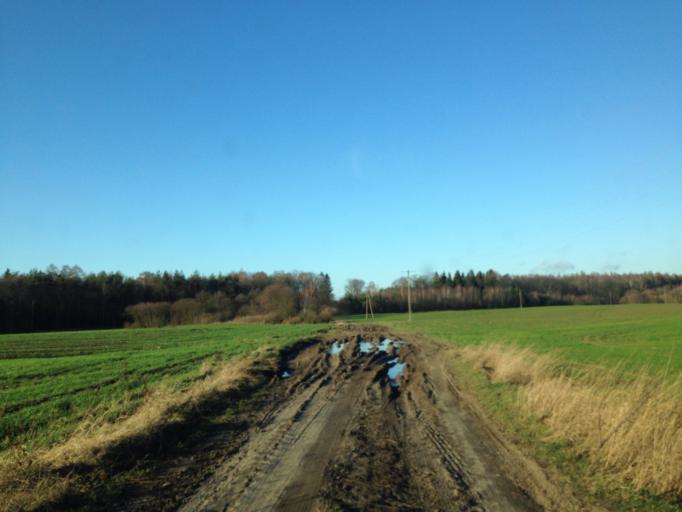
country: PL
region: Pomeranian Voivodeship
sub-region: Powiat kwidzynski
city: Gardeja
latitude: 53.6304
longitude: 19.0293
